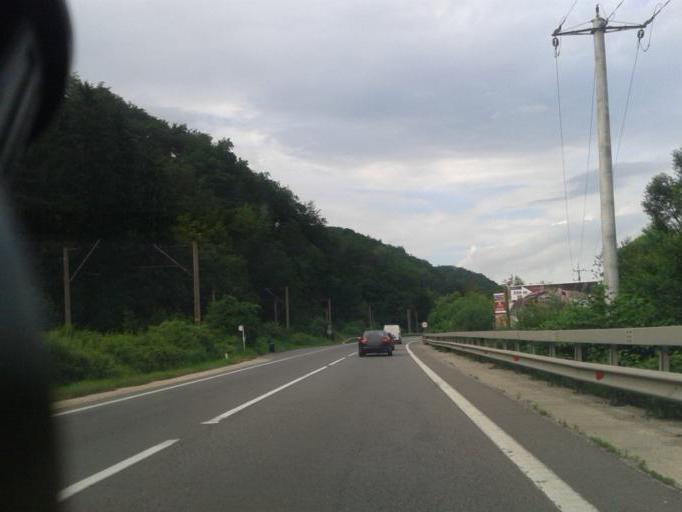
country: RO
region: Brasov
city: Brasov
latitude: 45.5937
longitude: 25.6344
